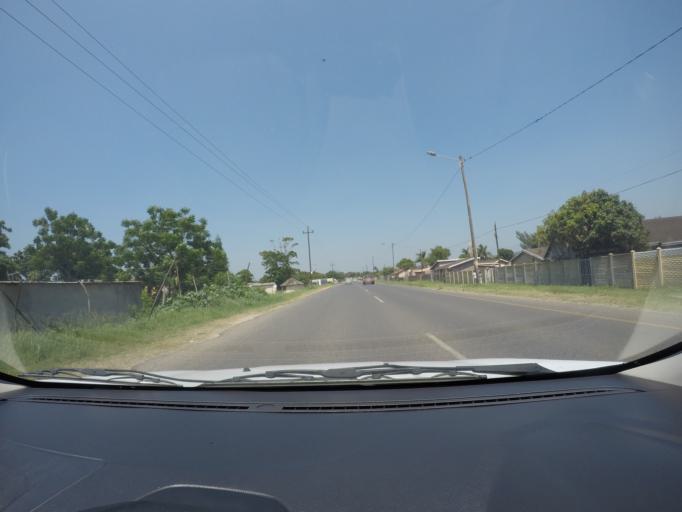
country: ZA
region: KwaZulu-Natal
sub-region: uThungulu District Municipality
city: eSikhawini
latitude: -28.8710
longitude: 31.9239
